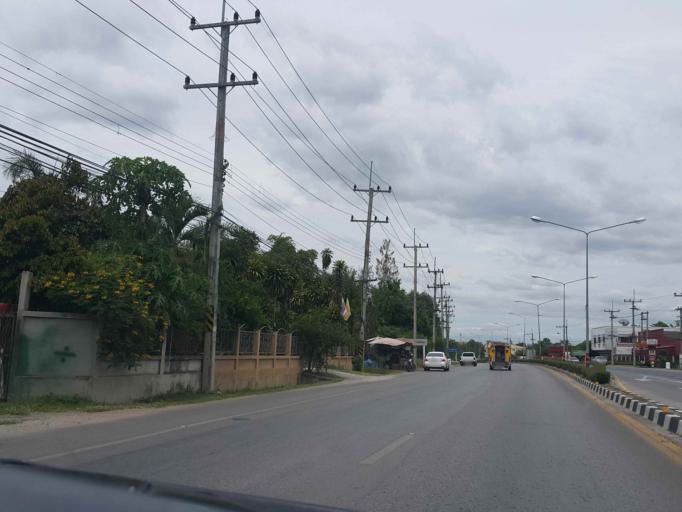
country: TH
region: Chiang Mai
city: San Pa Tong
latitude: 18.5820
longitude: 98.8836
